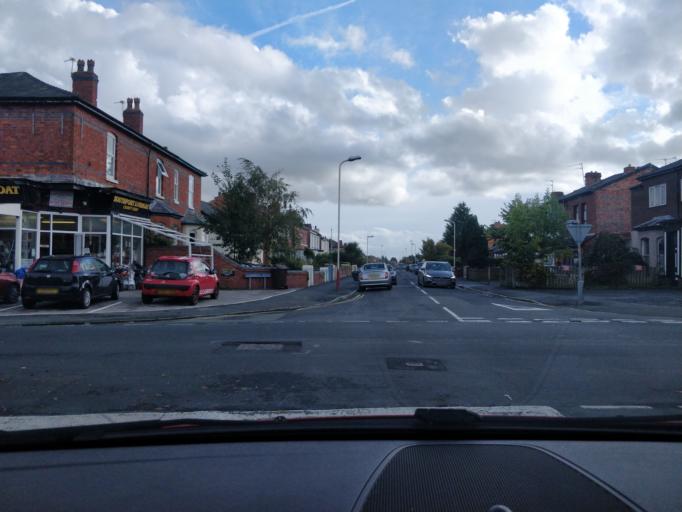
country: GB
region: England
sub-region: Sefton
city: Southport
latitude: 53.6321
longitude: -3.0095
